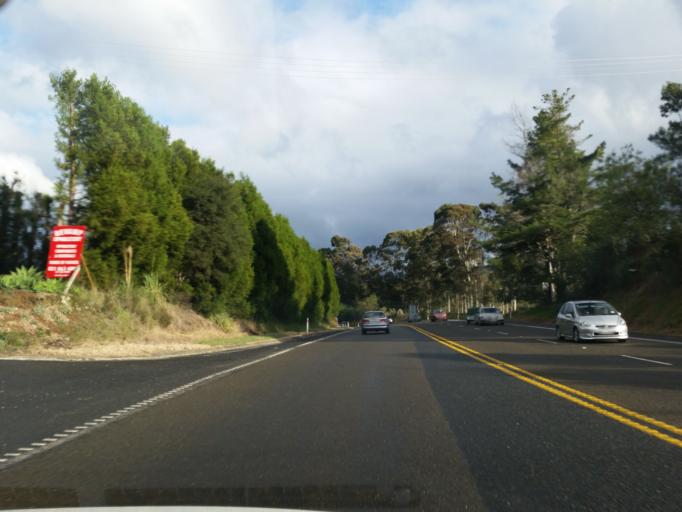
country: NZ
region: Bay of Plenty
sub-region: Western Bay of Plenty District
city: Katikati
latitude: -37.6295
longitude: 175.9572
